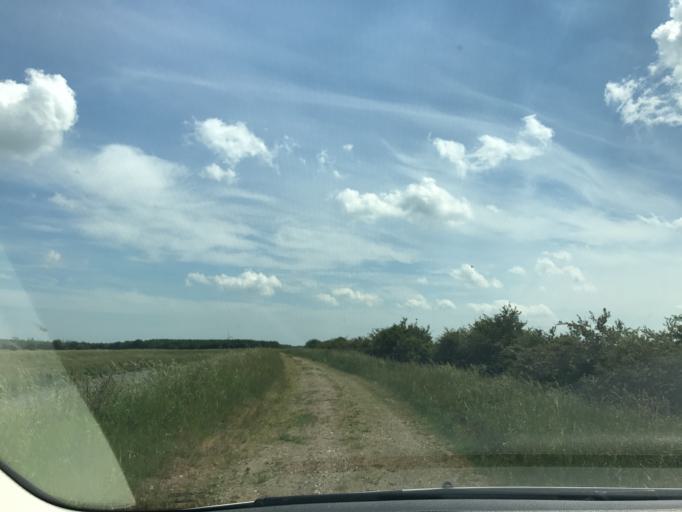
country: DE
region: Schleswig-Holstein
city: Ellhoft
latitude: 54.9245
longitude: 8.9420
